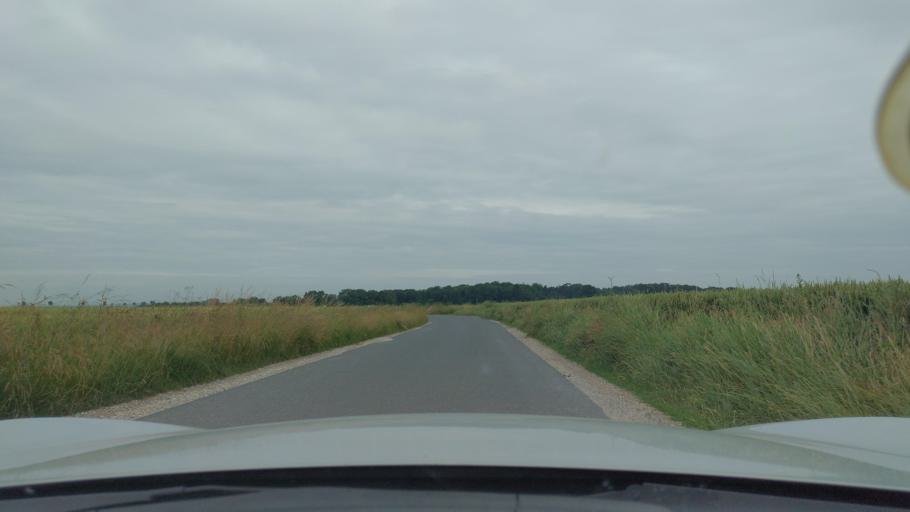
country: FR
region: Picardie
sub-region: Departement de l'Oise
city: Betz
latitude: 49.1398
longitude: 2.9721
